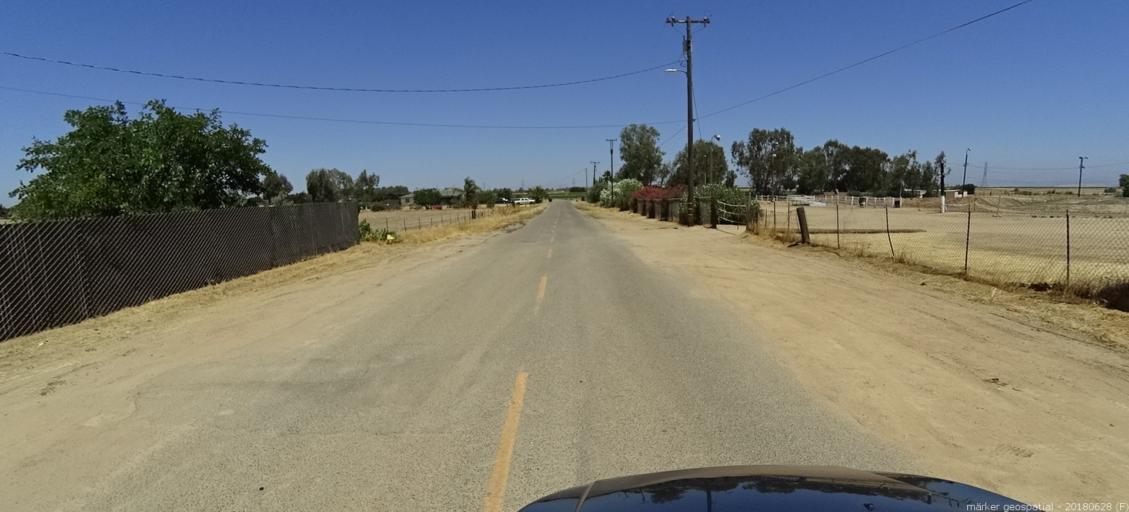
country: US
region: California
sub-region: Madera County
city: Parksdale
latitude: 36.9506
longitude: -120.0149
